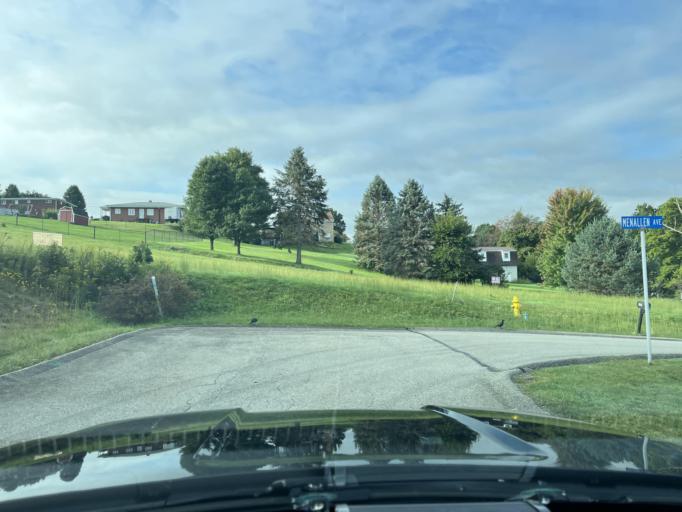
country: US
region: Pennsylvania
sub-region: Fayette County
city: Leith-Hatfield
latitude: 39.8783
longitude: -79.7414
